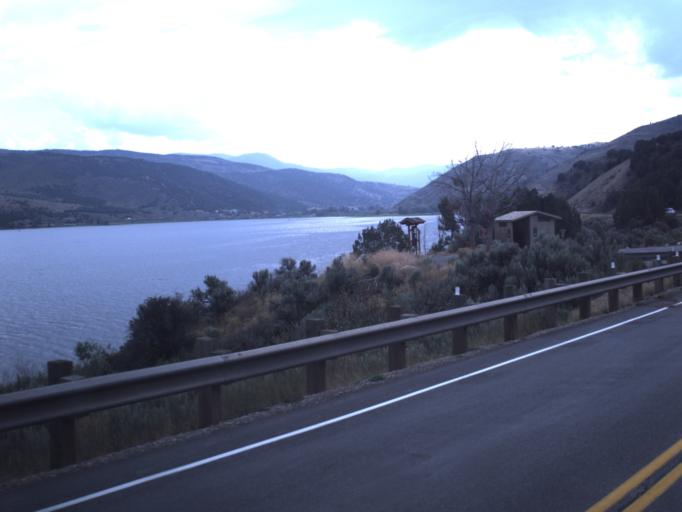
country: US
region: Utah
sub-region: Summit County
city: Oakley
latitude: 40.7641
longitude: -111.3979
